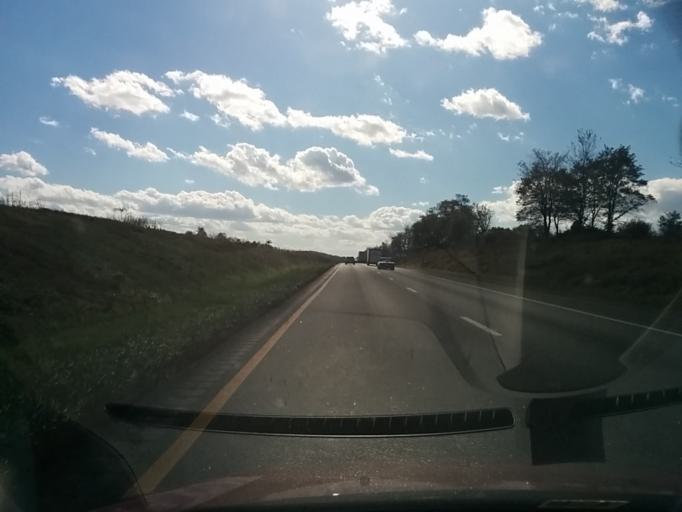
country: US
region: Virginia
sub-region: Augusta County
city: Stuarts Draft
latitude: 37.9607
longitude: -79.2028
